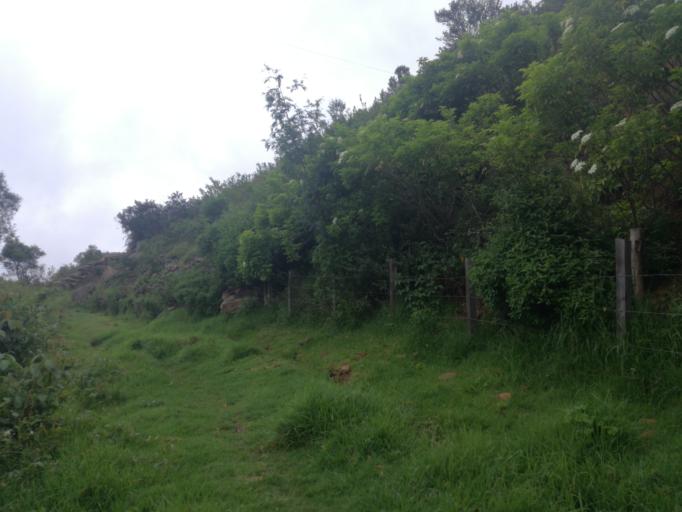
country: CO
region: Boyaca
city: Socha Viejo
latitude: 5.9995
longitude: -72.6868
